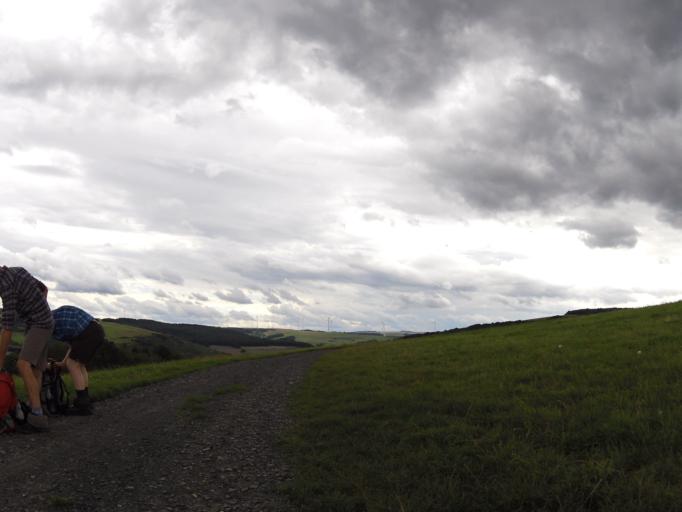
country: DE
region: Rheinland-Pfalz
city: Odernheim
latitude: 49.7683
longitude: 7.6917
